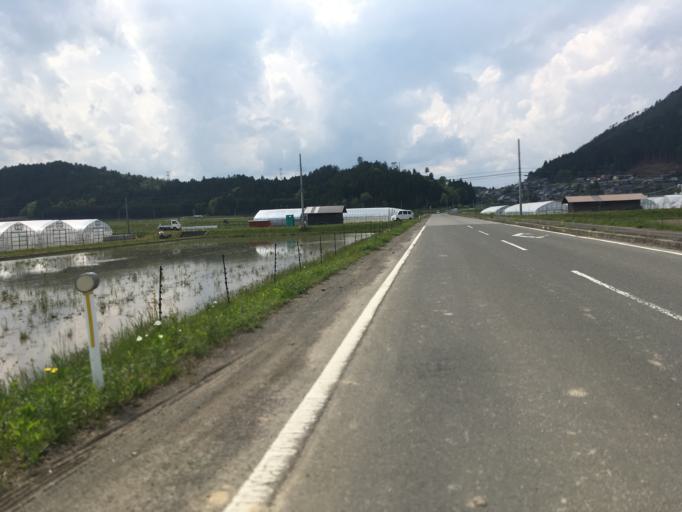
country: JP
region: Kyoto
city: Kameoka
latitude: 35.1043
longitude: 135.5865
